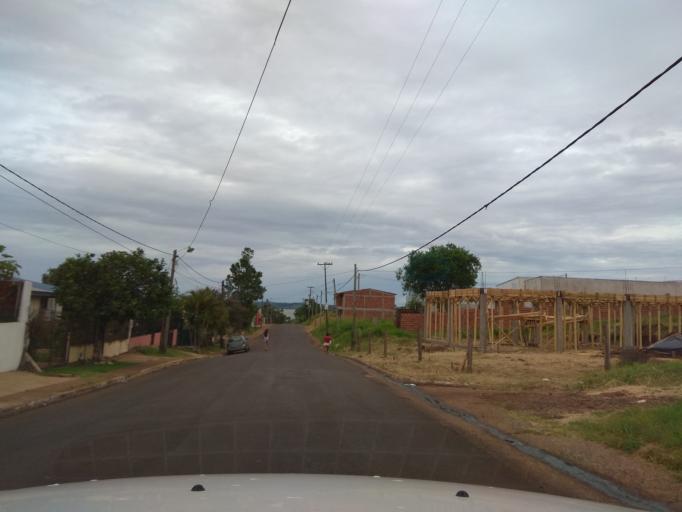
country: AR
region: Misiones
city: Garupa
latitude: -27.4490
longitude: -55.8554
